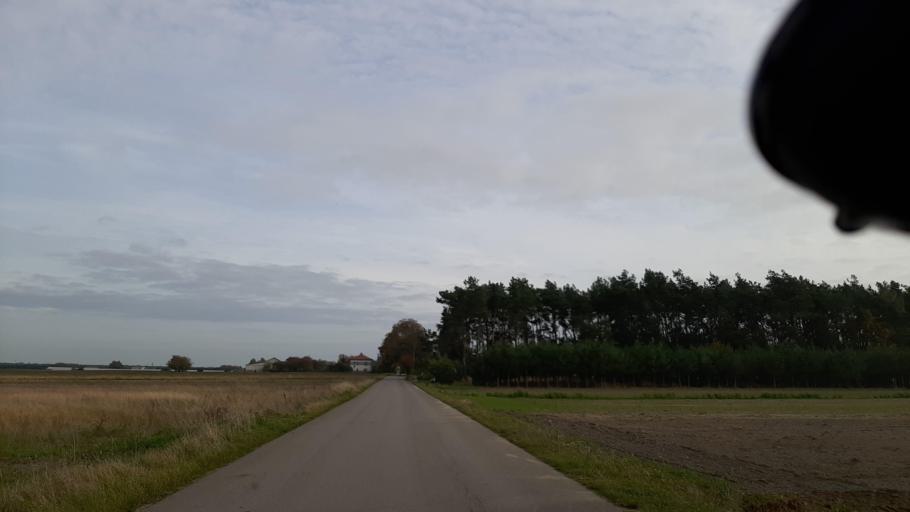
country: PL
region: Lublin Voivodeship
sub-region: Powiat lubelski
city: Garbow
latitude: 51.3975
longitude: 22.3374
